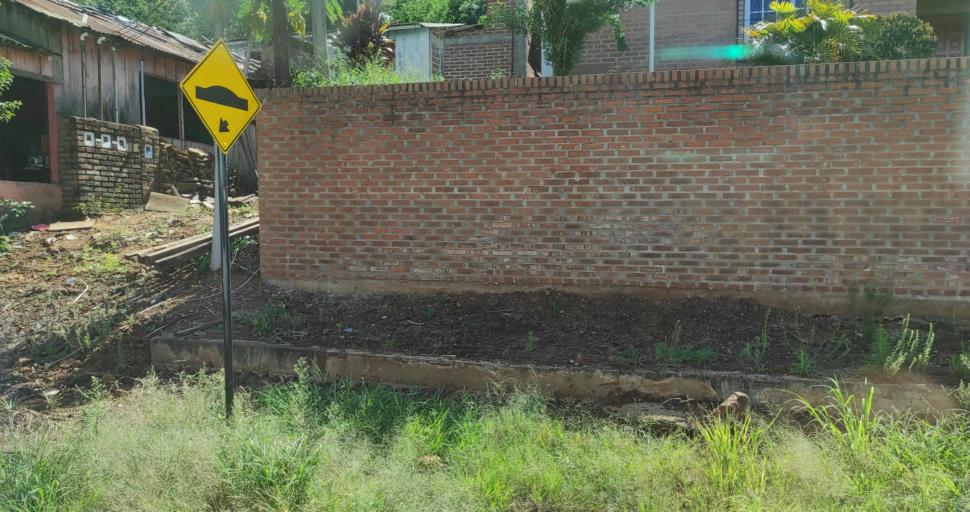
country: AR
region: Misiones
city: El Soberbio
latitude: -27.2904
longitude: -54.1986
